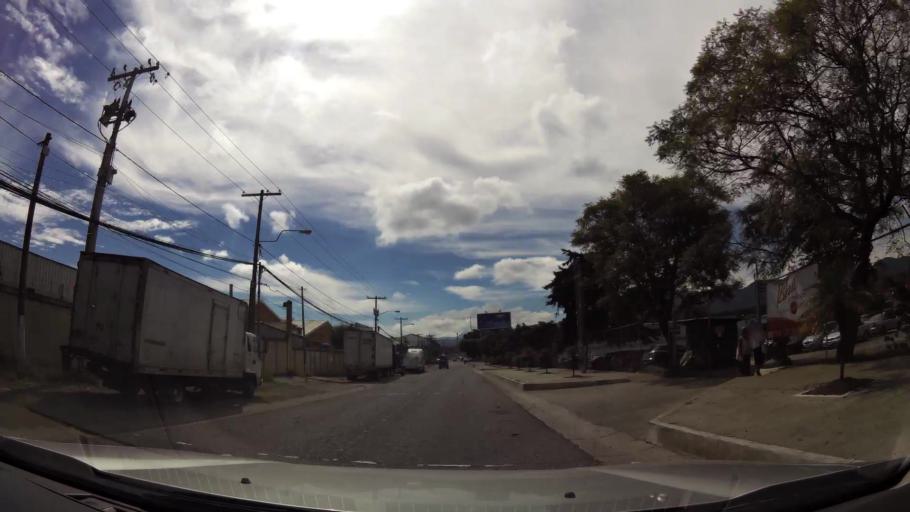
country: GT
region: Guatemala
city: Mixco
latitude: 14.6407
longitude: -90.5841
